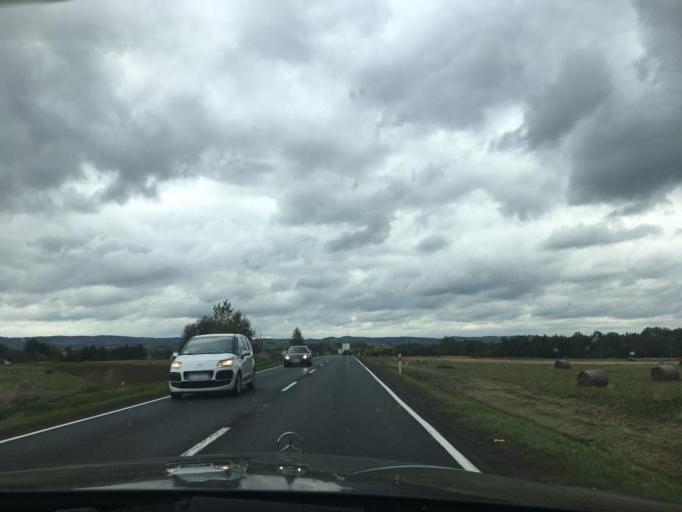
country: PL
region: Subcarpathian Voivodeship
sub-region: Powiat krosnienski
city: Kroscienko Wyzne
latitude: 49.6652
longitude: 21.8409
